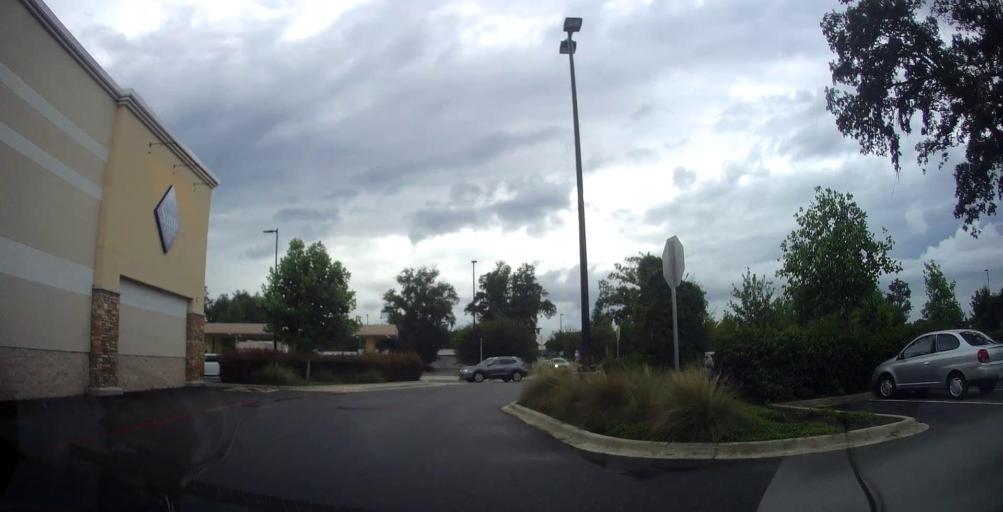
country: US
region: Florida
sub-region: Alachua County
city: Gainesville
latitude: 29.6243
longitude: -82.3848
